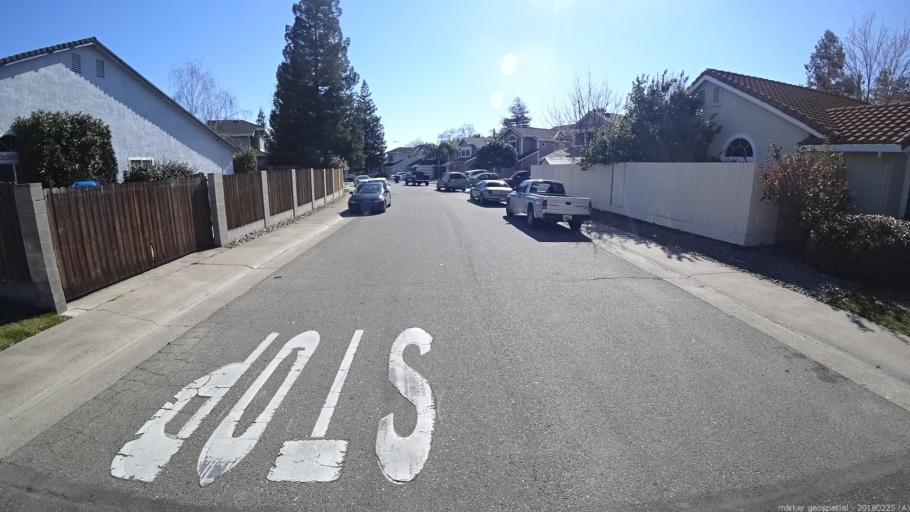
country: US
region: California
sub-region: Sacramento County
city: North Highlands
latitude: 38.7238
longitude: -121.3881
